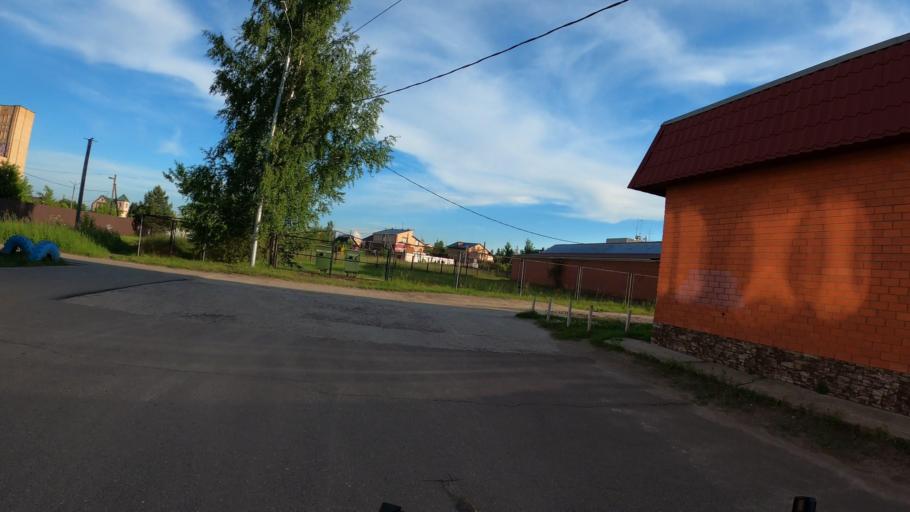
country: RU
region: Moskovskaya
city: Ashitkovo
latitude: 55.4357
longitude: 38.5846
